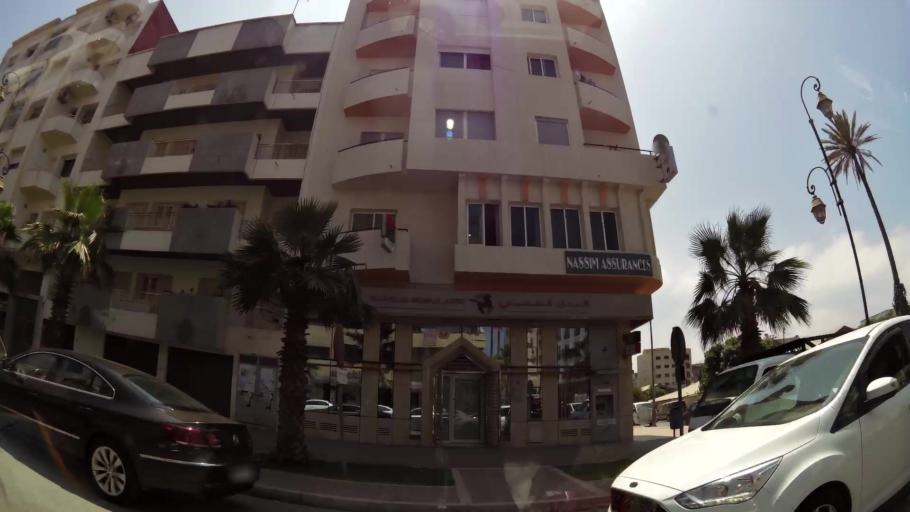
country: MA
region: Rabat-Sale-Zemmour-Zaer
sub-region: Rabat
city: Rabat
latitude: 34.0222
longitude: -6.8465
